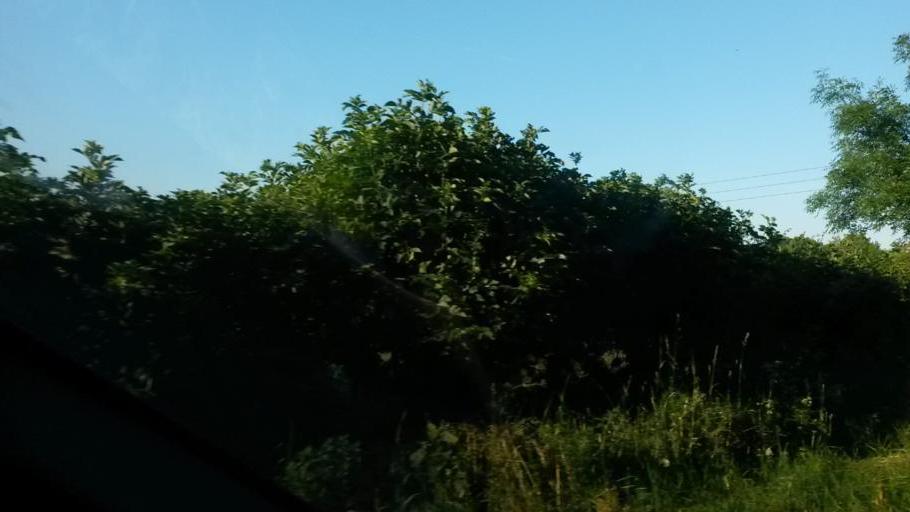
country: IE
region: Leinster
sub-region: An Mhi
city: Ashbourne
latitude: 53.5780
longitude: -6.3758
